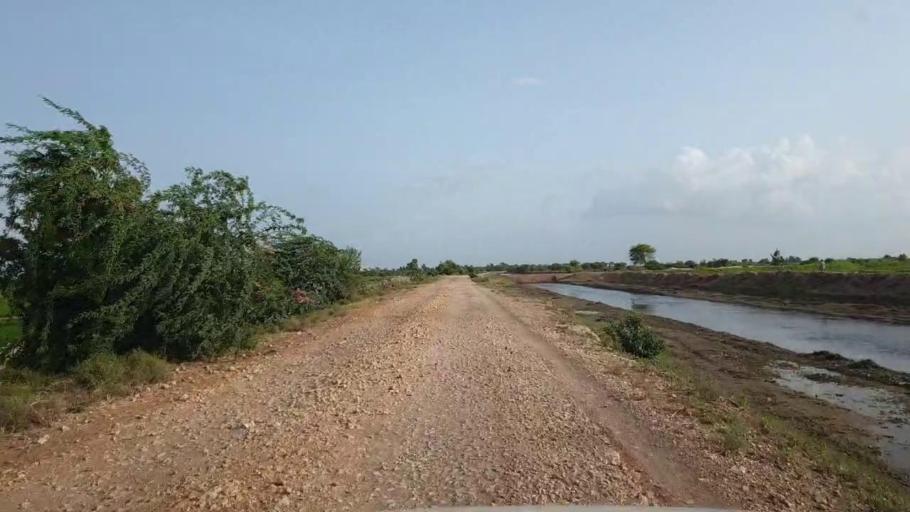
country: PK
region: Sindh
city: Kario
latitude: 24.8459
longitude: 68.6523
